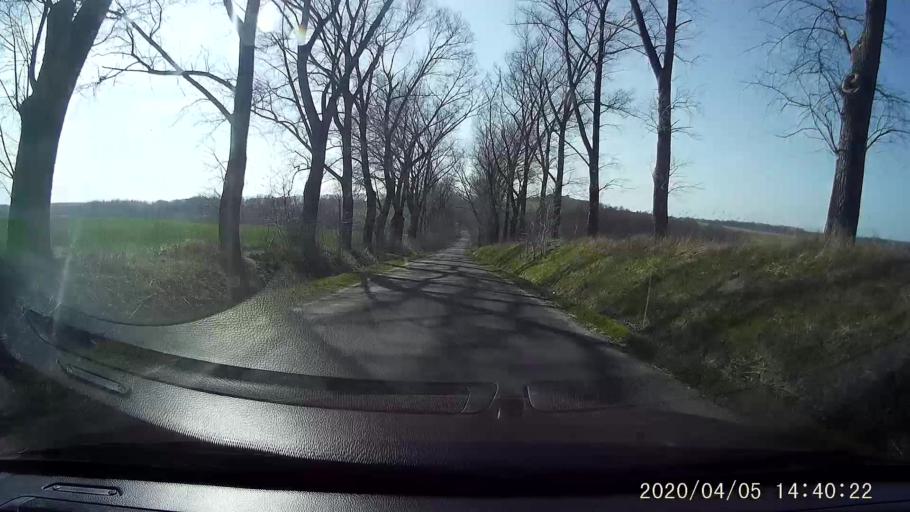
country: PL
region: Lower Silesian Voivodeship
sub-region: Powiat lubanski
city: Siekierczyn
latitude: 51.0606
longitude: 15.1644
